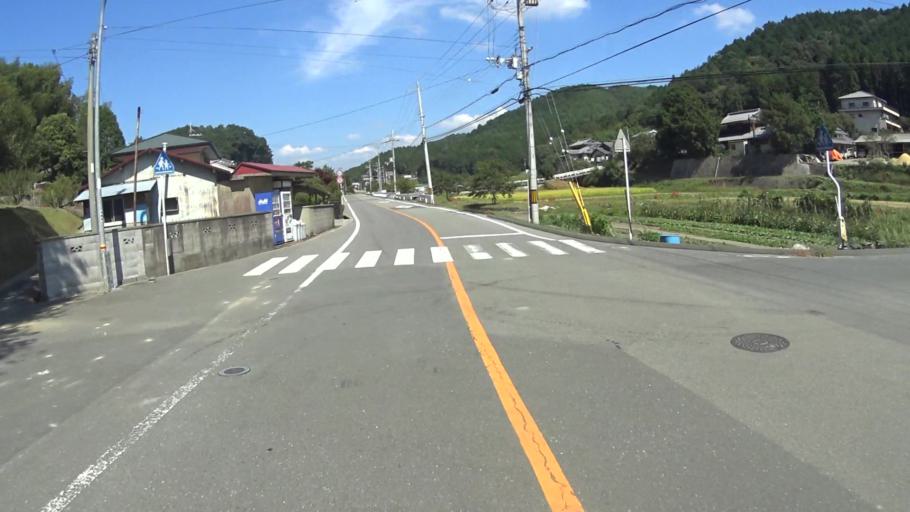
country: JP
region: Kyoto
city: Kameoka
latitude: 34.9641
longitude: 135.5005
